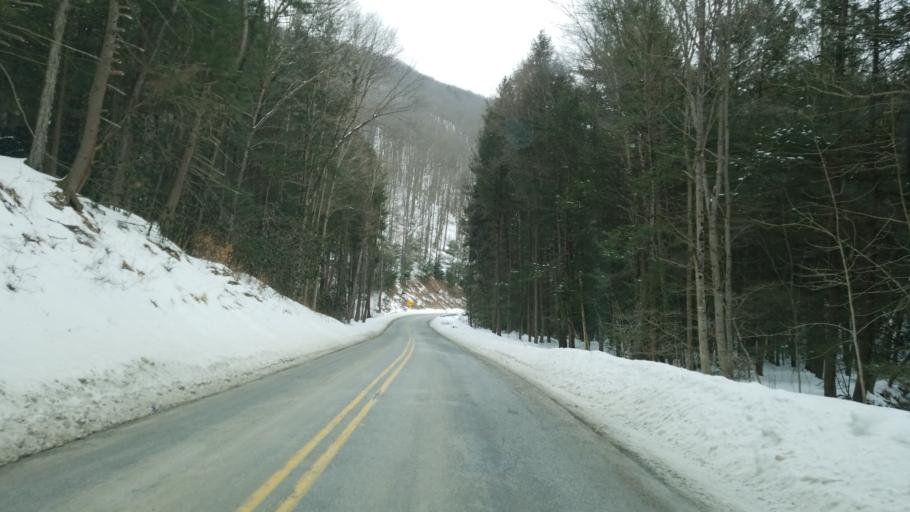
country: US
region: Pennsylvania
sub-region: Cameron County
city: Emporium
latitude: 41.2655
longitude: -78.1549
